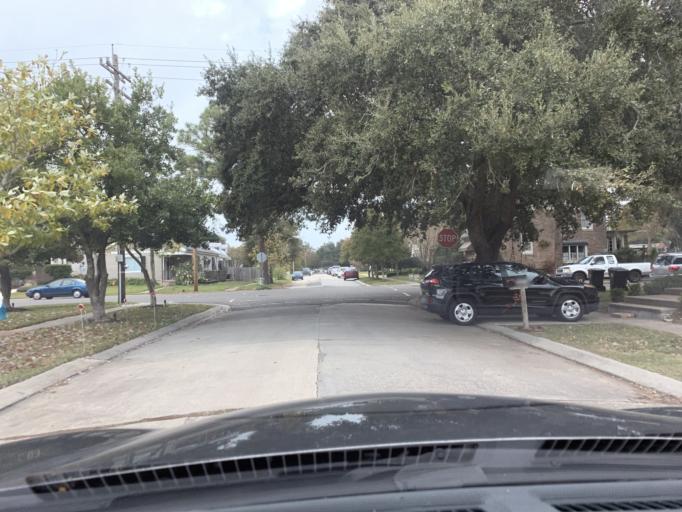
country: US
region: Louisiana
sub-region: Jefferson Parish
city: Metairie
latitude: 30.0116
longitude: -90.1029
